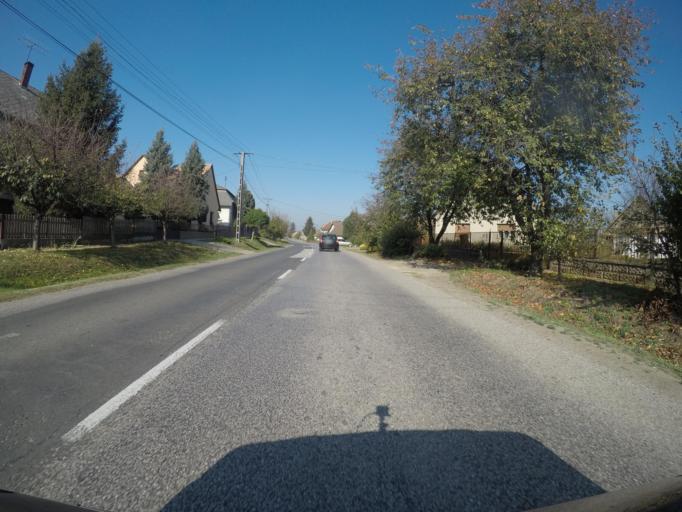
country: HU
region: Tolna
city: Szedres
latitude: 46.4809
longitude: 18.6832
